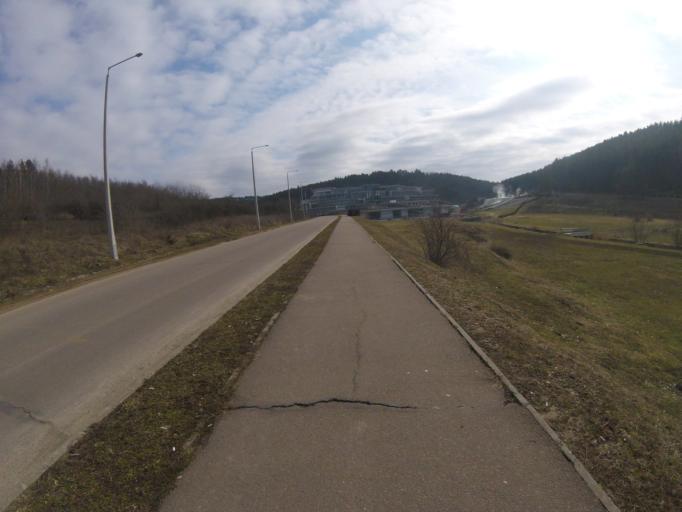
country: HU
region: Heves
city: Egerszalok
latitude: 47.8547
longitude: 20.3316
